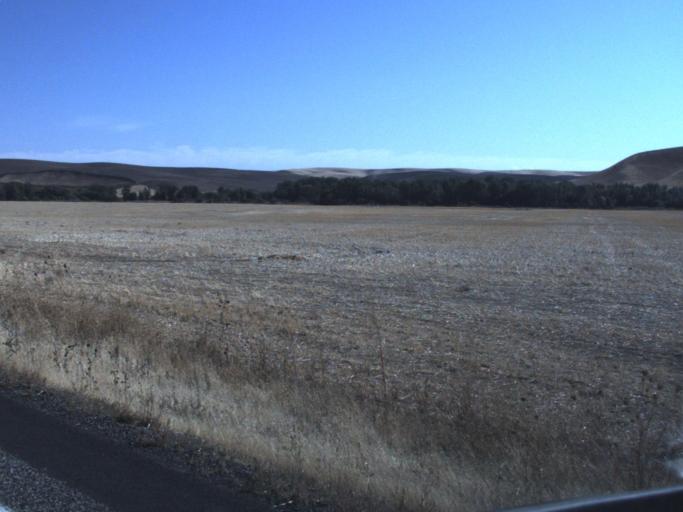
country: US
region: Washington
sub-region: Walla Walla County
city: Walla Walla
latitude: 46.2992
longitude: -118.3999
